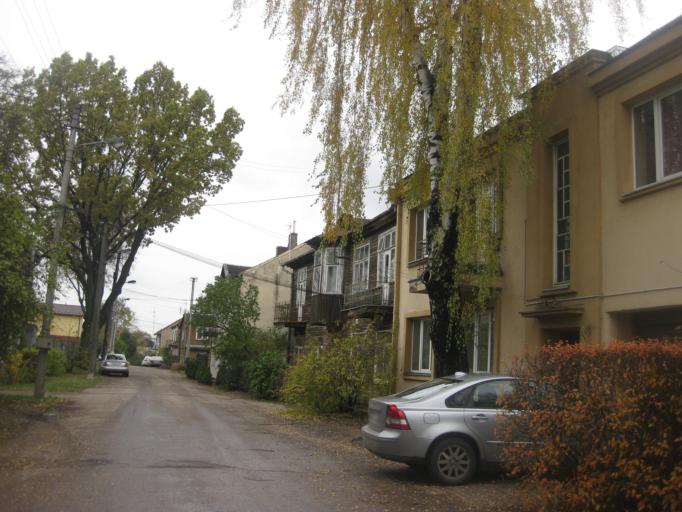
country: LT
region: Kauno apskritis
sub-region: Kaunas
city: Kaunas
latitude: 54.9071
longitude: 23.9108
